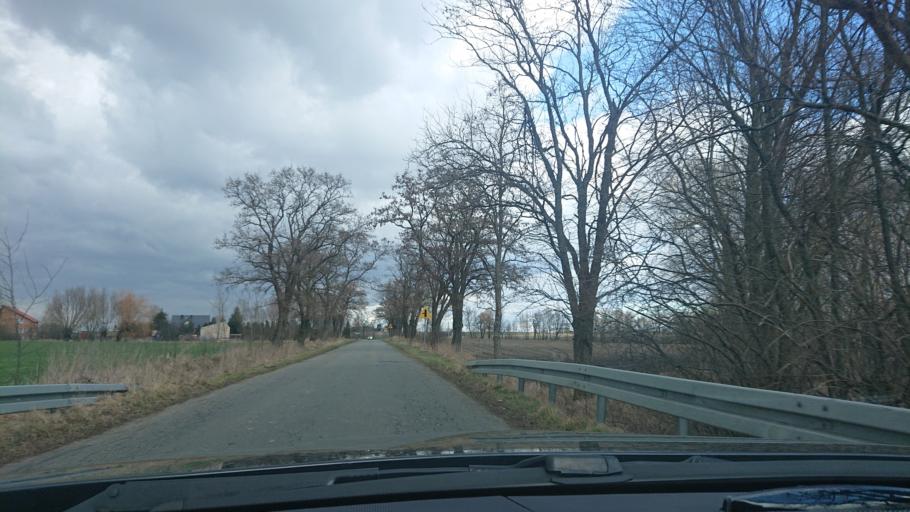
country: PL
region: Greater Poland Voivodeship
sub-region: Powiat gnieznienski
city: Trzemeszno
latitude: 52.5800
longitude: 17.7118
